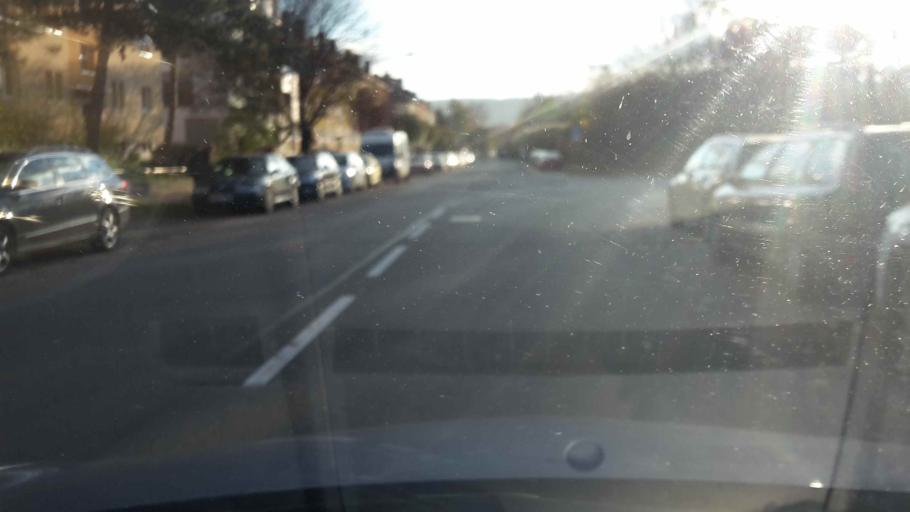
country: CZ
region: South Moravian
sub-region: Mesto Brno
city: Brno
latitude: 49.2112
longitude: 16.5745
